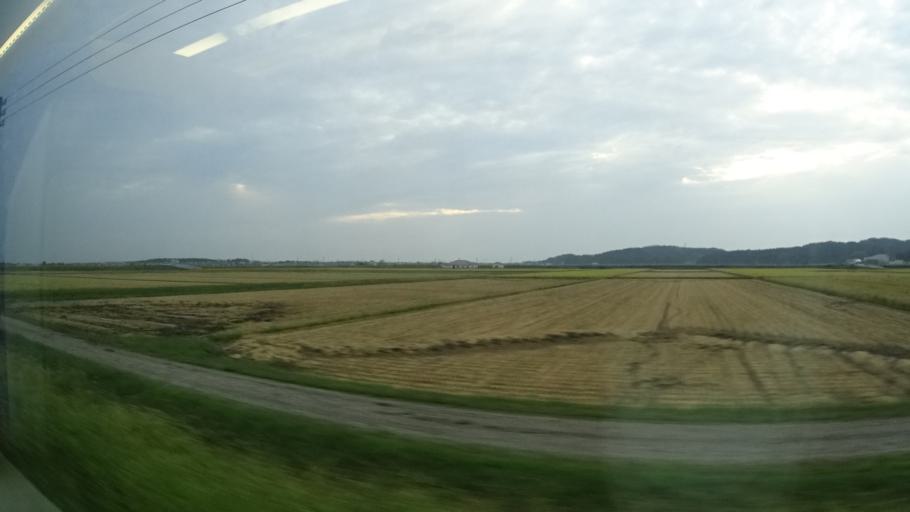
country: JP
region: Niigata
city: Murakami
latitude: 38.2015
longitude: 139.4600
